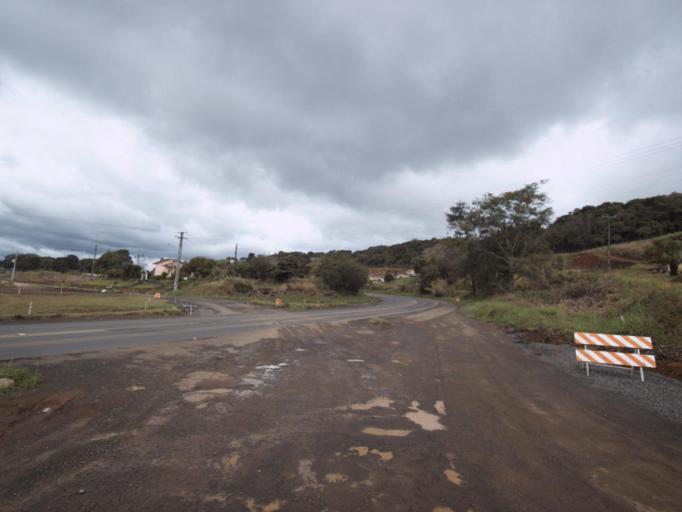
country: BR
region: Santa Catarina
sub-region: Concordia
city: Concordia
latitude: -27.2290
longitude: -51.9528
